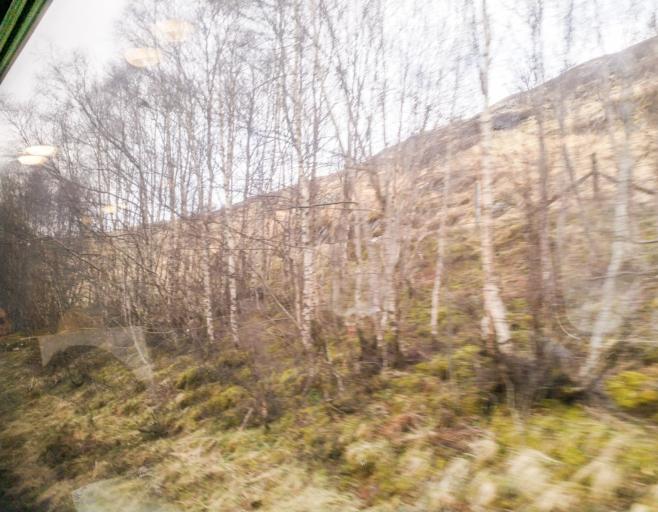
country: GB
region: Scotland
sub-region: Highland
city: Spean Bridge
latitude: 56.7908
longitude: -4.7273
